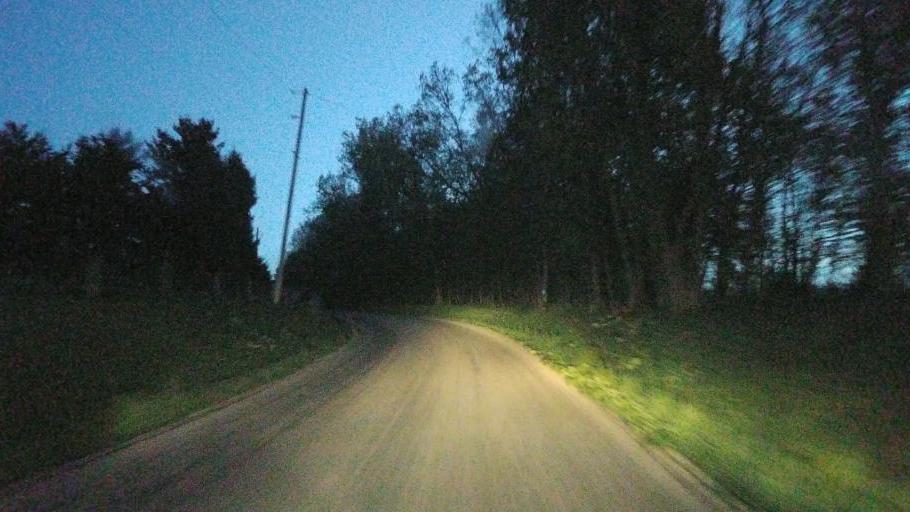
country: US
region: Ohio
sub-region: Knox County
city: Danville
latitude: 40.5159
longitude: -82.3812
